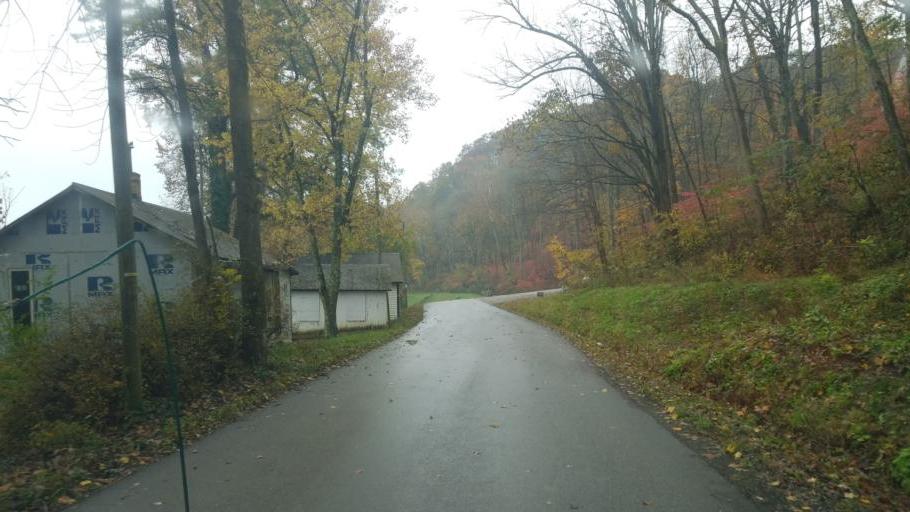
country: US
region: Ohio
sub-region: Washington County
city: Beverly
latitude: 39.5216
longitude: -81.7526
